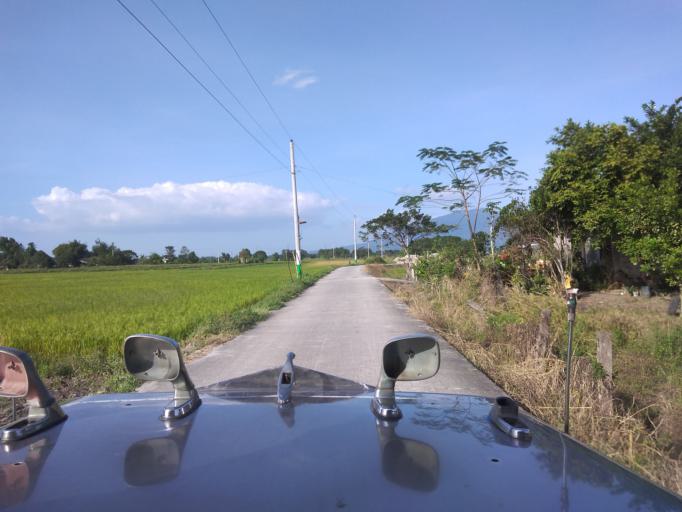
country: PH
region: Central Luzon
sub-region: Province of Pampanga
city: Bulaon
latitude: 15.0976
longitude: 120.6941
